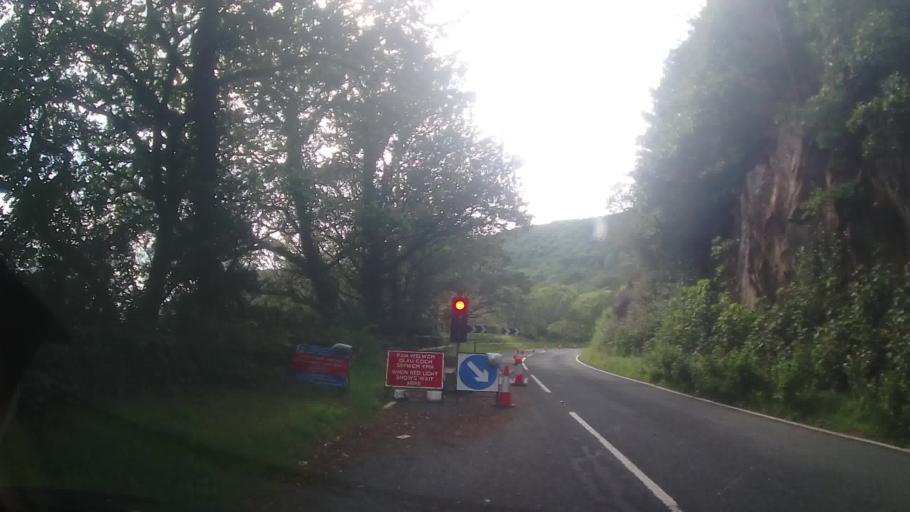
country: GB
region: Wales
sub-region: Gwynedd
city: Barmouth
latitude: 52.7364
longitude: -4.0194
